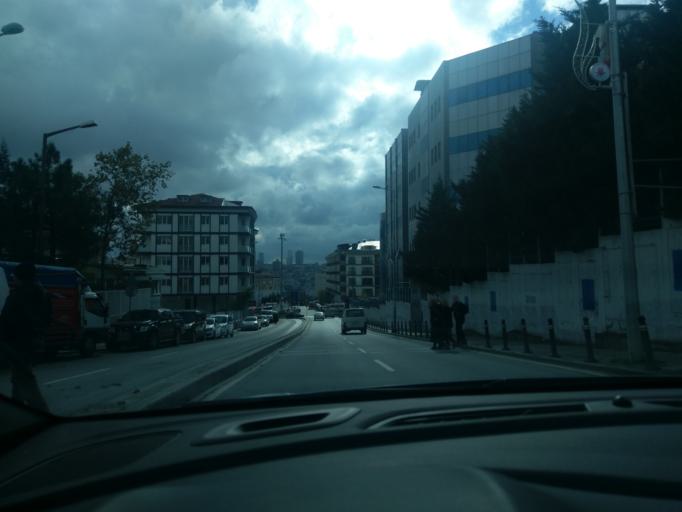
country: TR
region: Istanbul
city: Sisli
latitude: 41.0872
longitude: 28.9678
